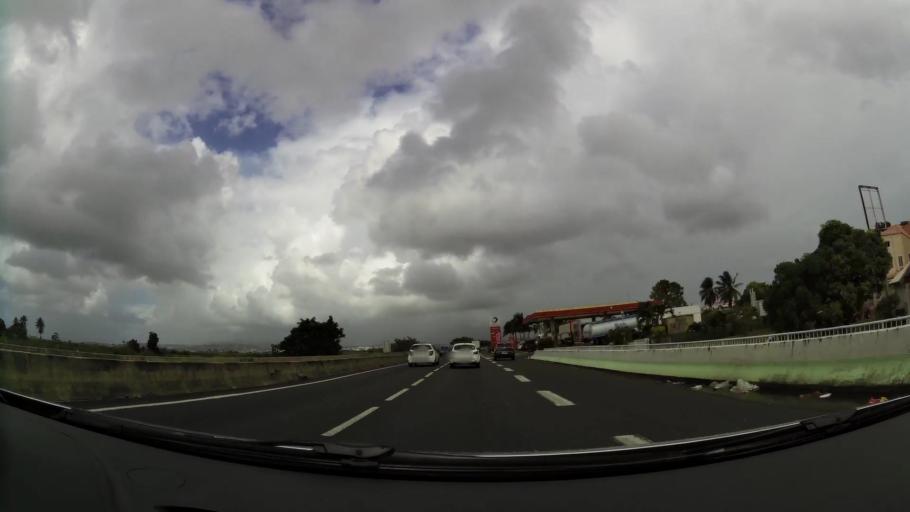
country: MQ
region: Martinique
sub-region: Martinique
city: Ducos
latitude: 14.5892
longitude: -60.9825
